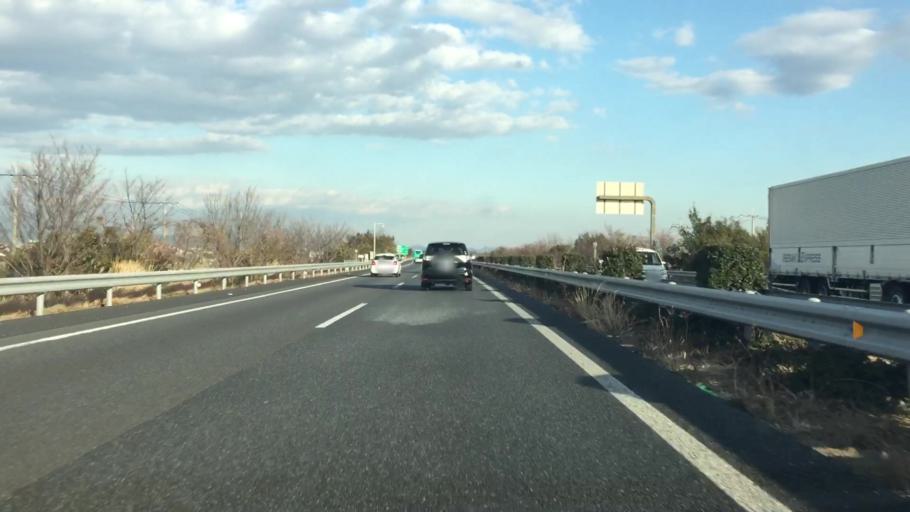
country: JP
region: Gunma
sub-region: Sawa-gun
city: Tamamura
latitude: 36.3348
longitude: 139.1070
